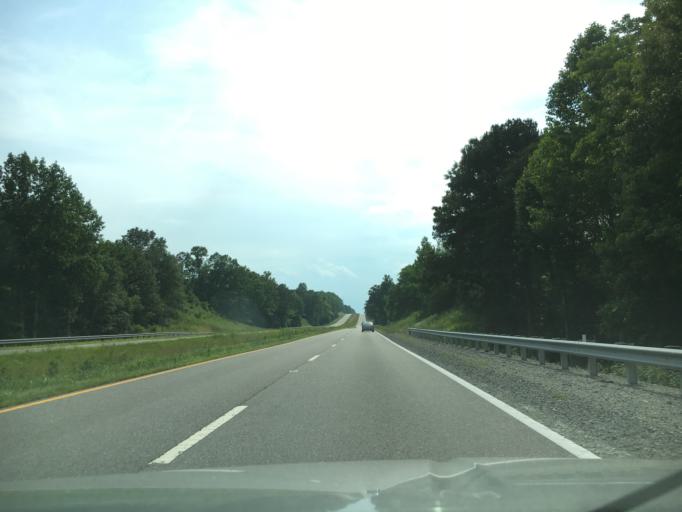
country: US
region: Virginia
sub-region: Halifax County
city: Halifax
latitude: 36.8237
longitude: -78.7075
